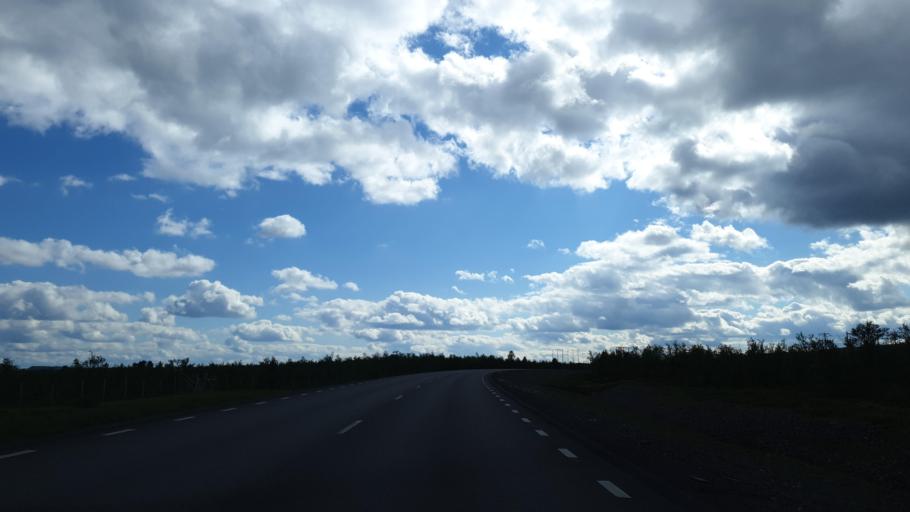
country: SE
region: Norrbotten
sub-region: Kiruna Kommun
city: Kiruna
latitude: 67.8299
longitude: 20.3018
